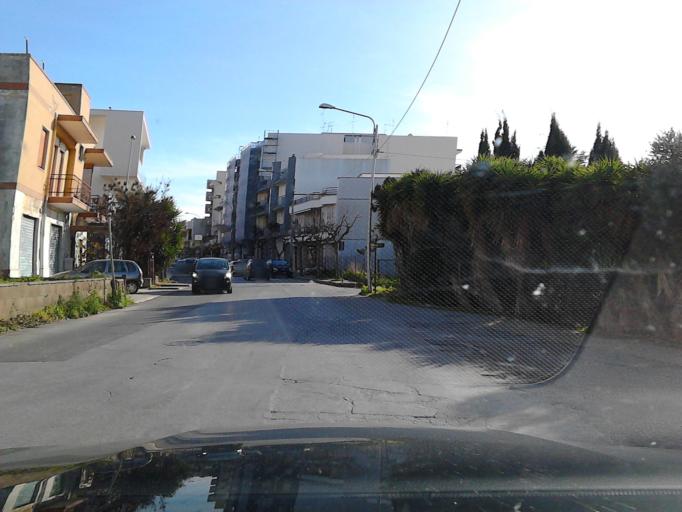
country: IT
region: Apulia
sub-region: Provincia di Bari
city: Rutigliano
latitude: 41.0181
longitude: 16.9990
